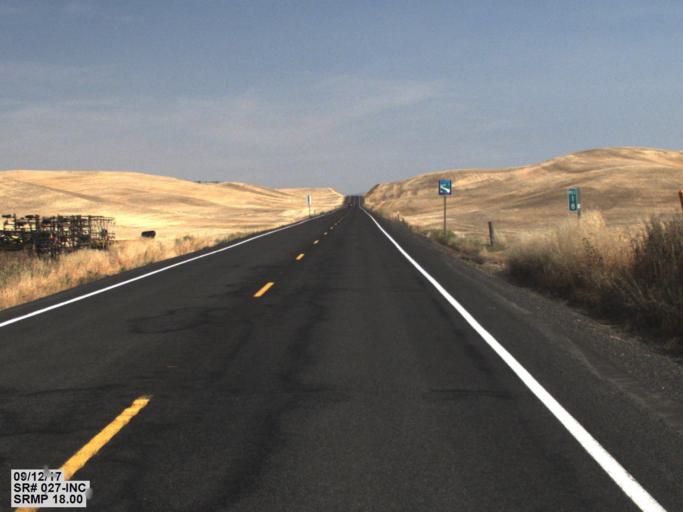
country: US
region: Washington
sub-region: Whitman County
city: Pullman
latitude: 46.9431
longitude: -117.0981
